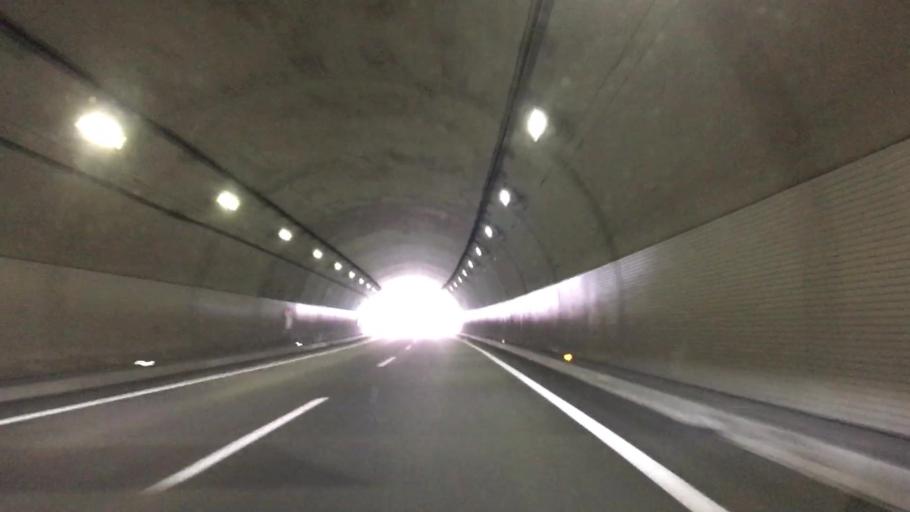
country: JP
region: Gifu
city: Tajimi
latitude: 35.2961
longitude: 137.1798
